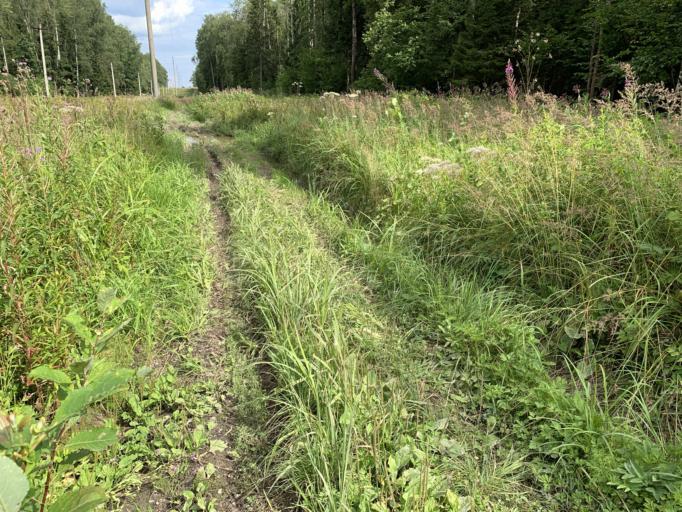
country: RU
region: Moskovskaya
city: Podosinki
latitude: 56.1819
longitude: 37.5699
